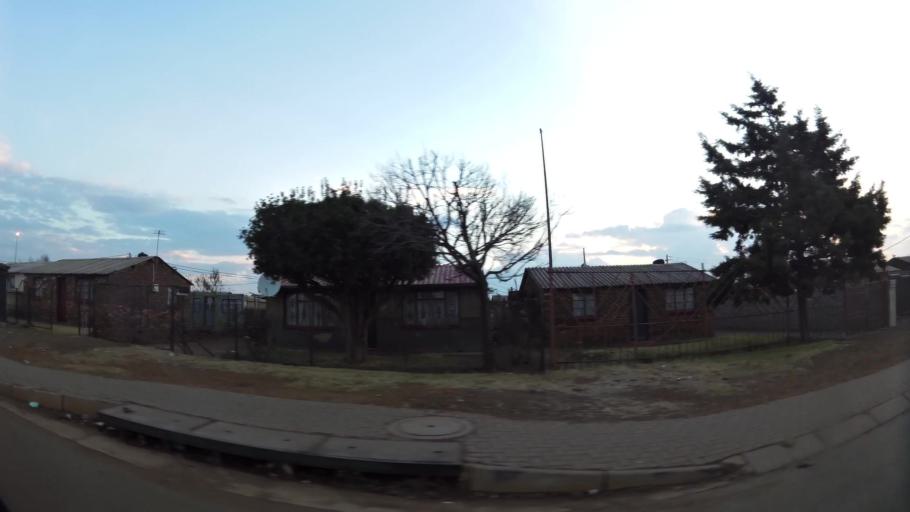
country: ZA
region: Gauteng
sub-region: City of Johannesburg Metropolitan Municipality
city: Orange Farm
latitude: -26.5504
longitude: 27.8730
